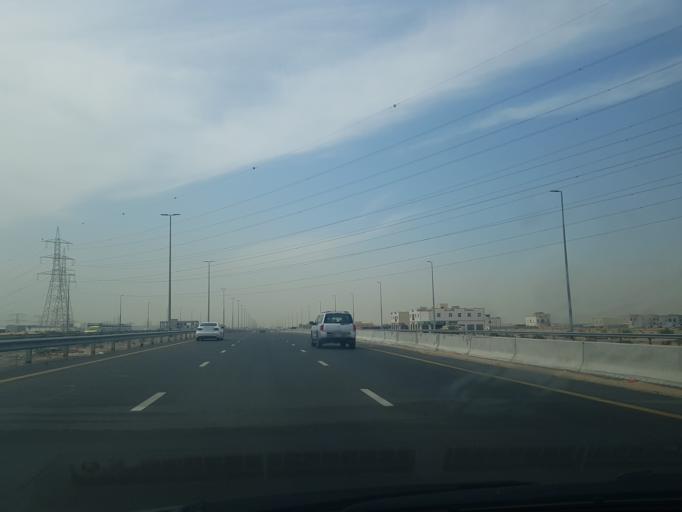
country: AE
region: Ash Shariqah
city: Sharjah
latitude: 25.2415
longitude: 55.5584
